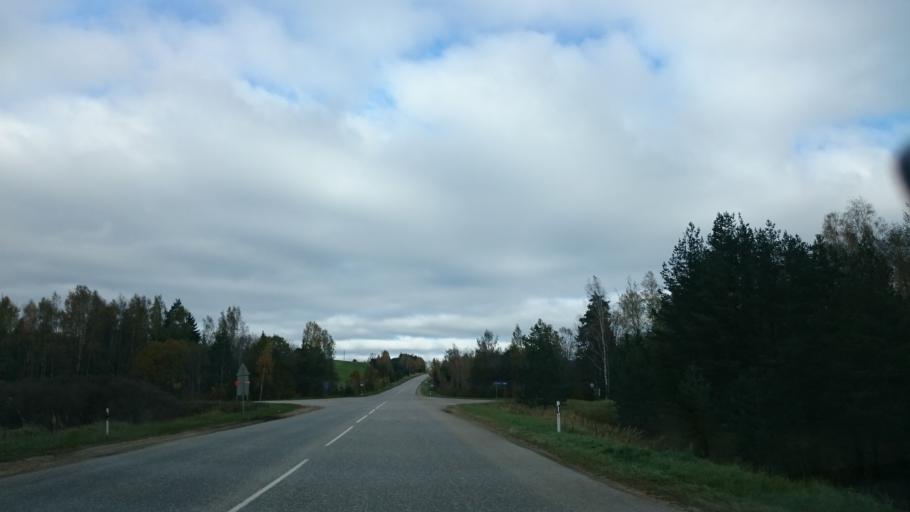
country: LV
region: Amatas Novads
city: Drabesi
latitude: 57.2600
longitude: 25.2671
